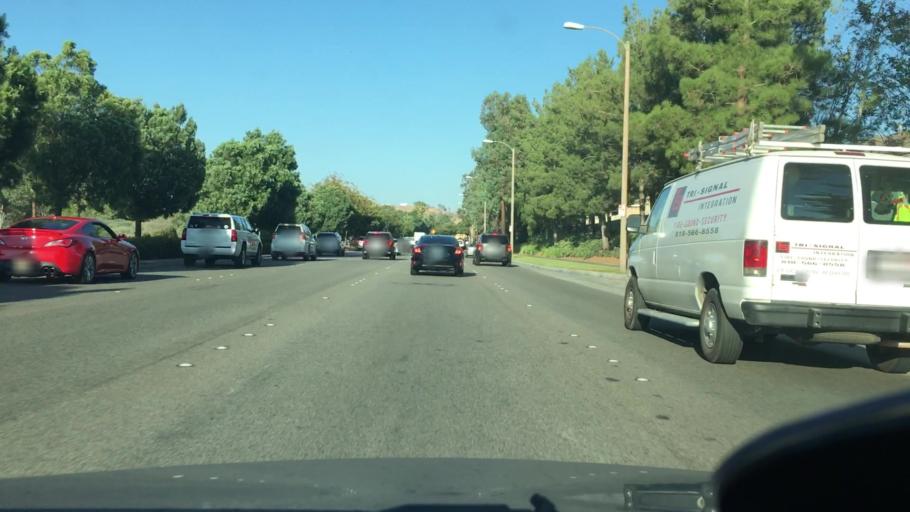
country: US
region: California
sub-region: Los Angeles County
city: Santa Clarita
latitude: 34.4282
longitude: -118.5446
